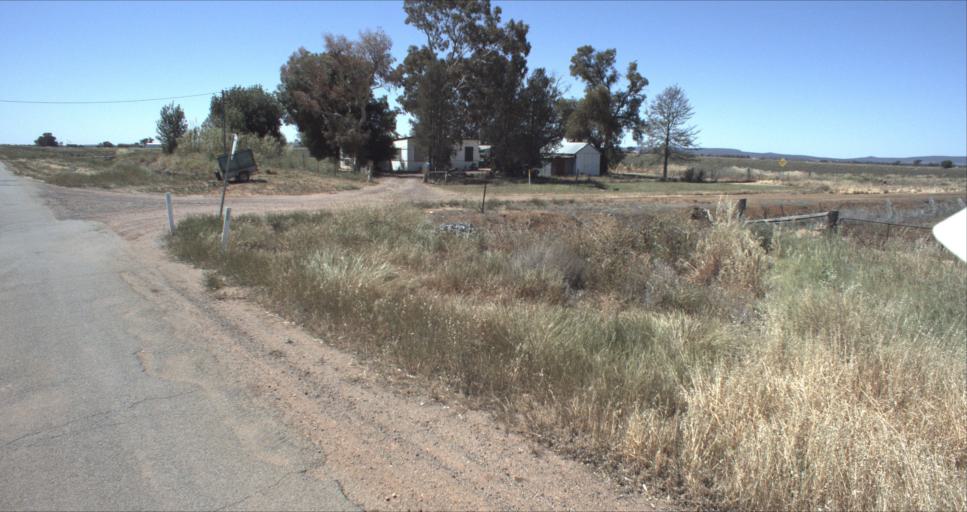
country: AU
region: New South Wales
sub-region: Leeton
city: Leeton
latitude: -34.5117
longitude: 146.3449
